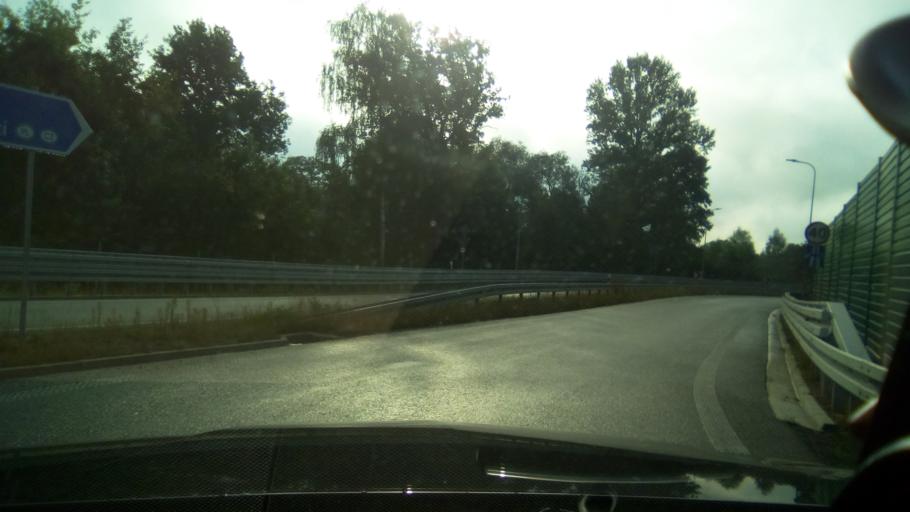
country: PL
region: Silesian Voivodeship
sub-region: Powiat czestochowski
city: Konopiska
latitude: 50.7494
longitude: 19.0474
